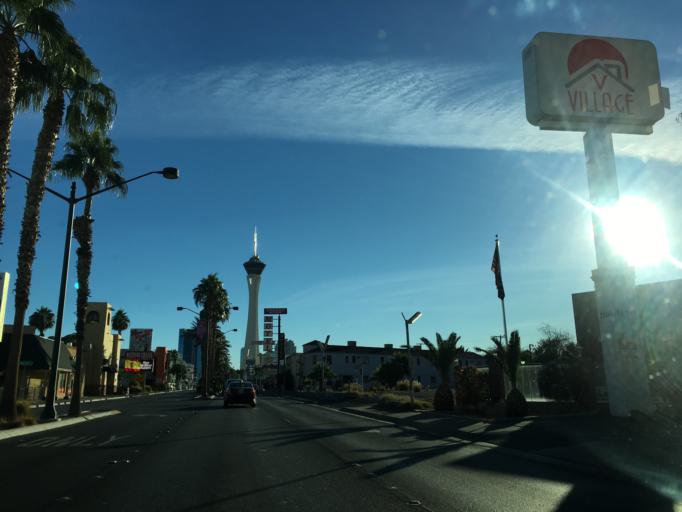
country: US
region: Nevada
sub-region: Clark County
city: Las Vegas
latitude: 36.1574
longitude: -115.1485
